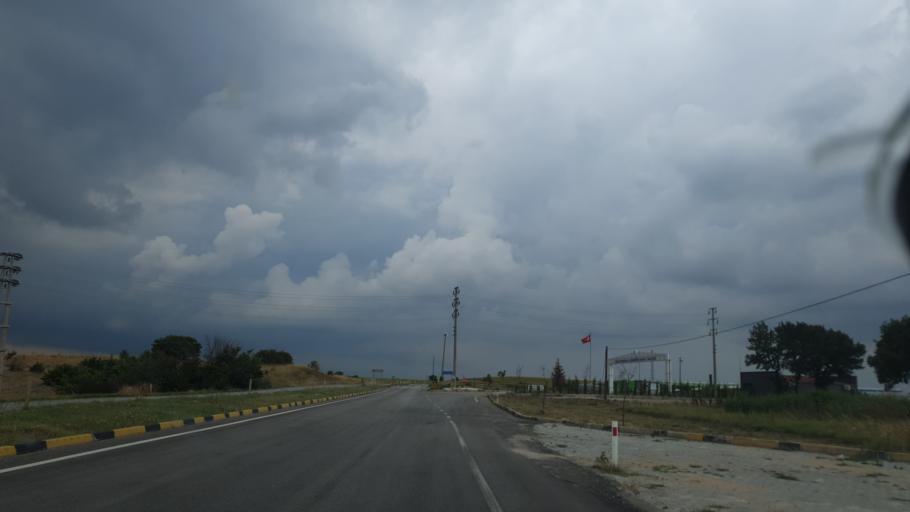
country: TR
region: Tekirdag
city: Hayrabolu
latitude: 41.2215
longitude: 27.0477
